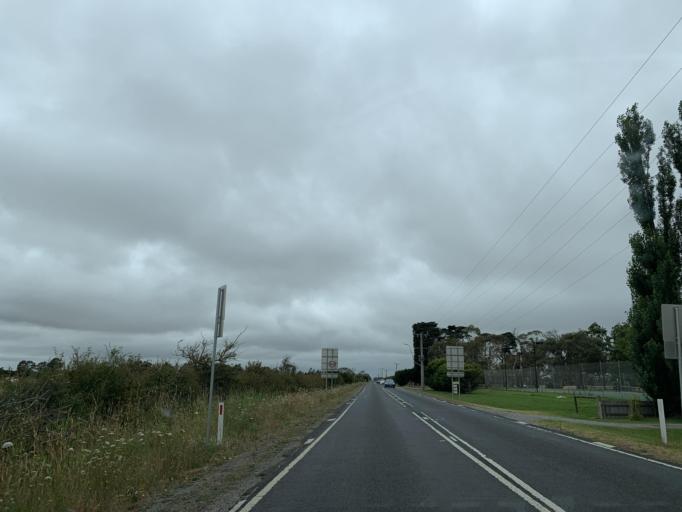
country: AU
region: Victoria
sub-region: Cardinia
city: Officer South
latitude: -38.1464
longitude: 145.4269
